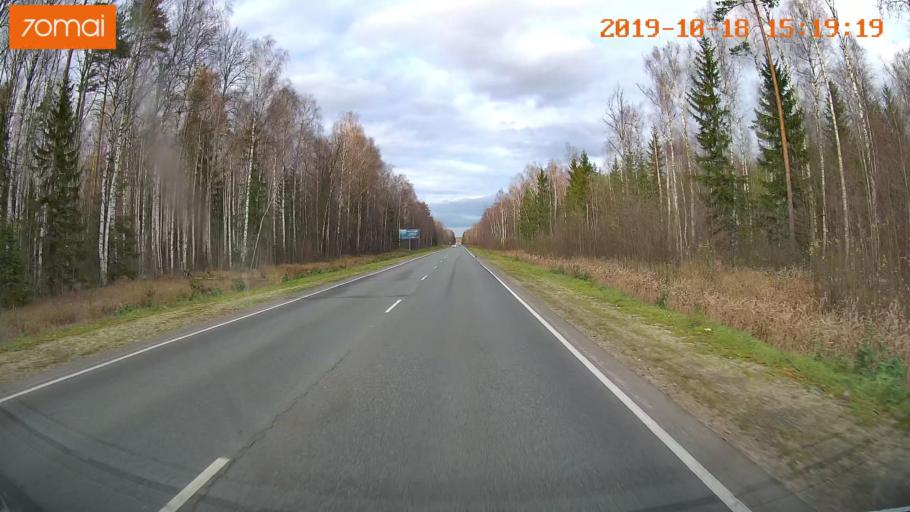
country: RU
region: Vladimir
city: Anopino
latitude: 55.6712
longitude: 40.7366
